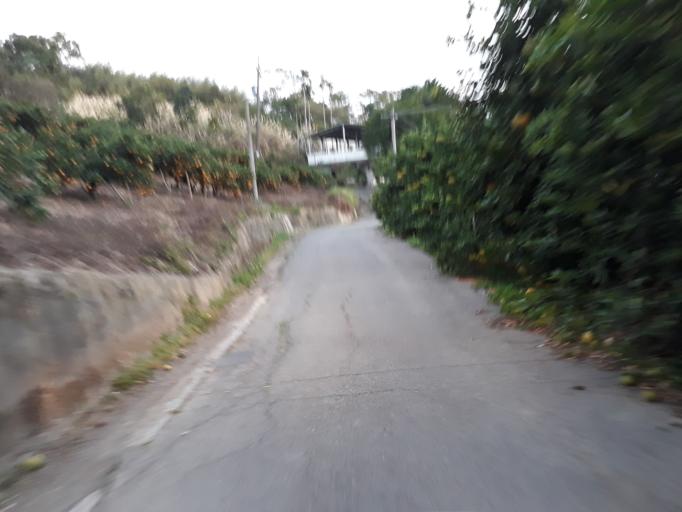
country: TW
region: Taiwan
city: Fengyuan
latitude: 24.3538
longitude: 120.8636
